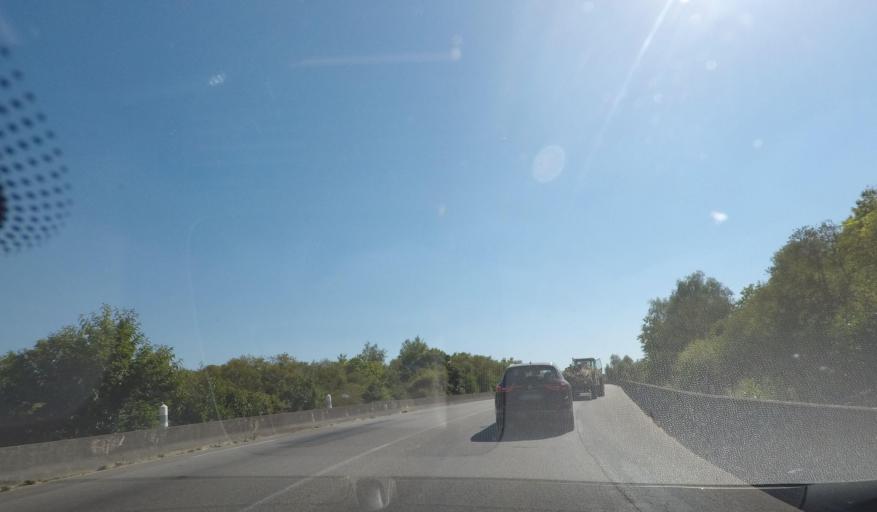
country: FR
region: Brittany
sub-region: Departement du Morbihan
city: Questembert
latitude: 47.6781
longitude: -2.4238
